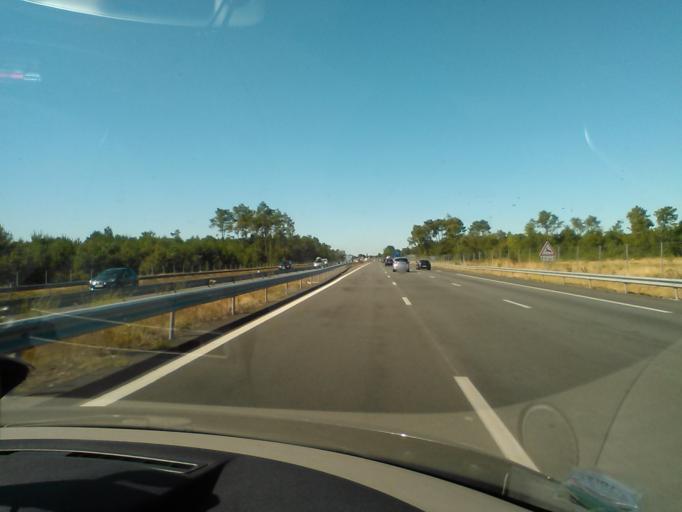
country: FR
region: Aquitaine
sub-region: Departement des Landes
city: Pissos
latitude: 44.3972
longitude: -0.8240
